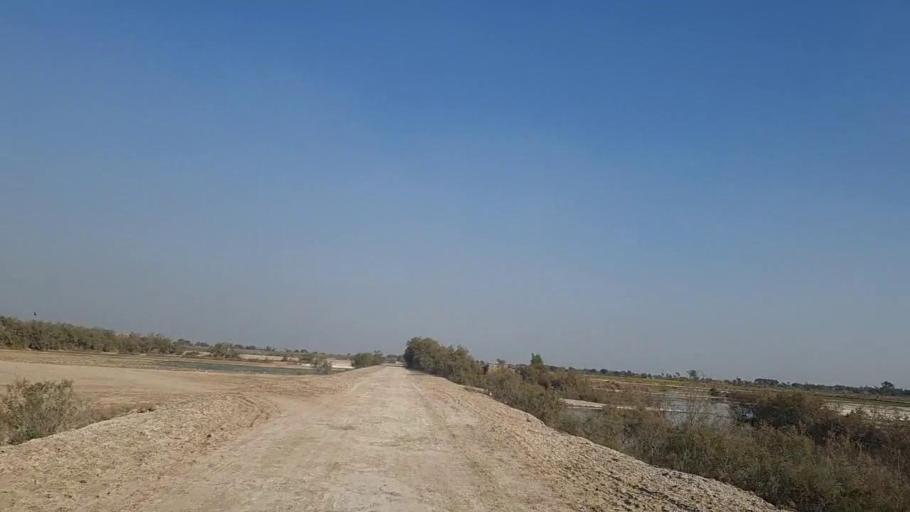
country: PK
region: Sindh
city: Daur
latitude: 26.3177
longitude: 68.1886
